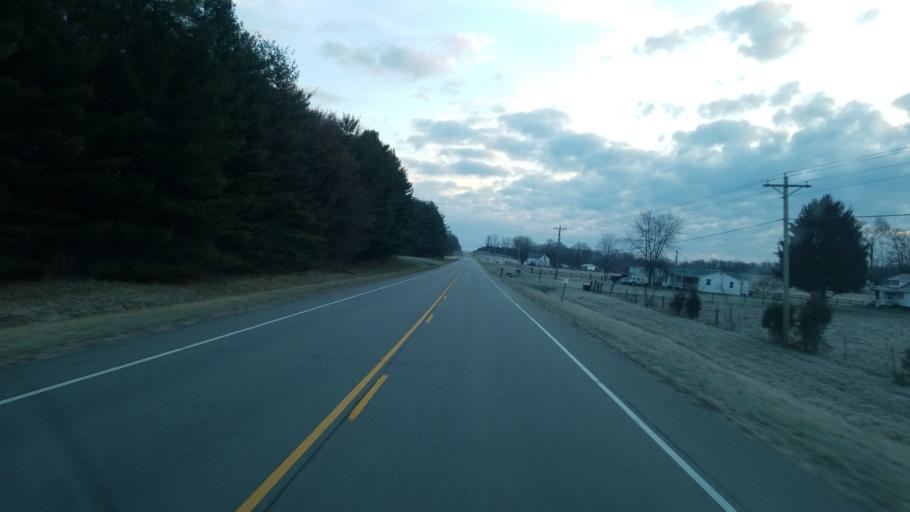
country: US
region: Ohio
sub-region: Highland County
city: Greenfield
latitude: 39.2283
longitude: -83.3750
